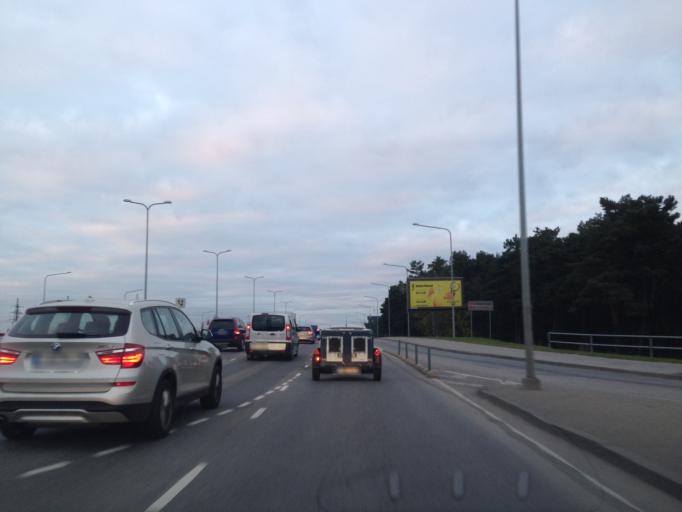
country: EE
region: Harju
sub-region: Tallinna linn
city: Tallinn
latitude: 59.3937
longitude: 24.7248
